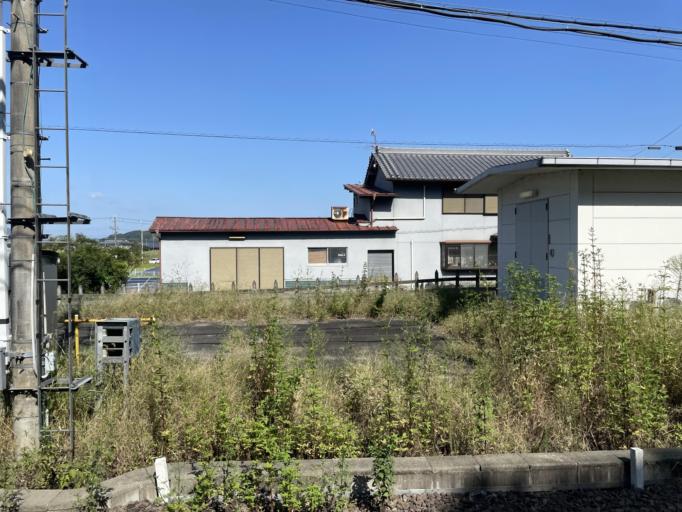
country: JP
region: Nara
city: Gose
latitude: 34.4417
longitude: 135.7757
